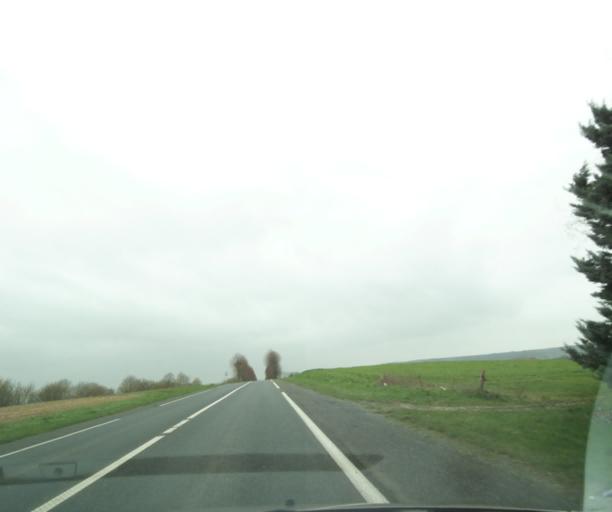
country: FR
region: Picardie
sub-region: Departement de l'Oise
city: Crisolles
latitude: 49.6083
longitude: 3.0178
